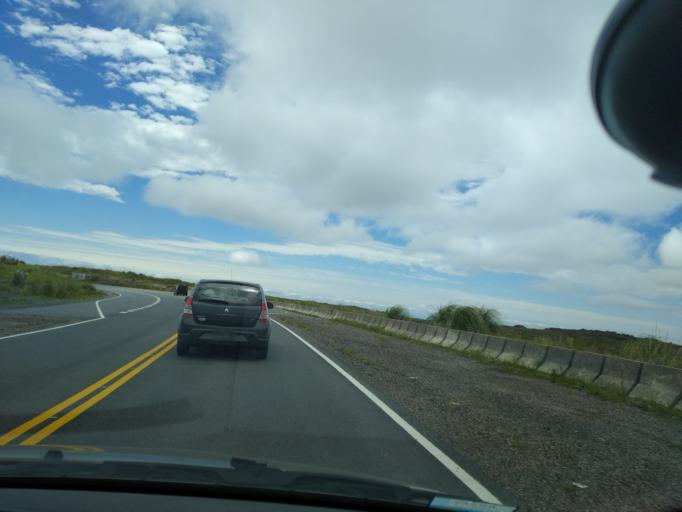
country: AR
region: Cordoba
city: Cuesta Blanca
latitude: -31.6130
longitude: -64.7143
